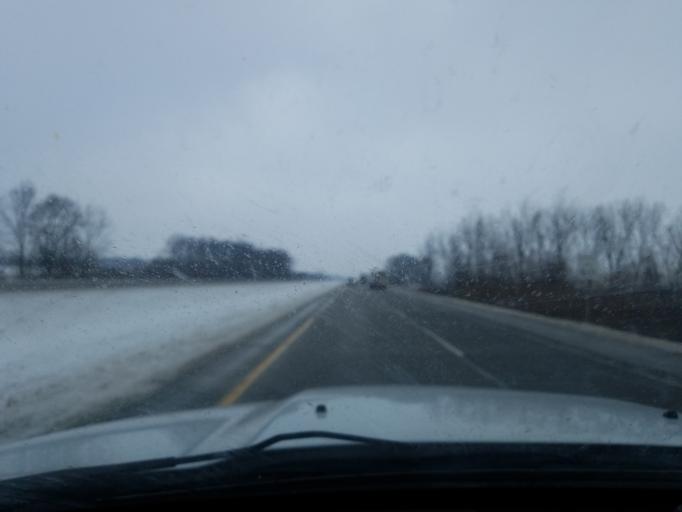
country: US
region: Indiana
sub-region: Marshall County
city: Argos
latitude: 41.1767
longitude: -86.2440
